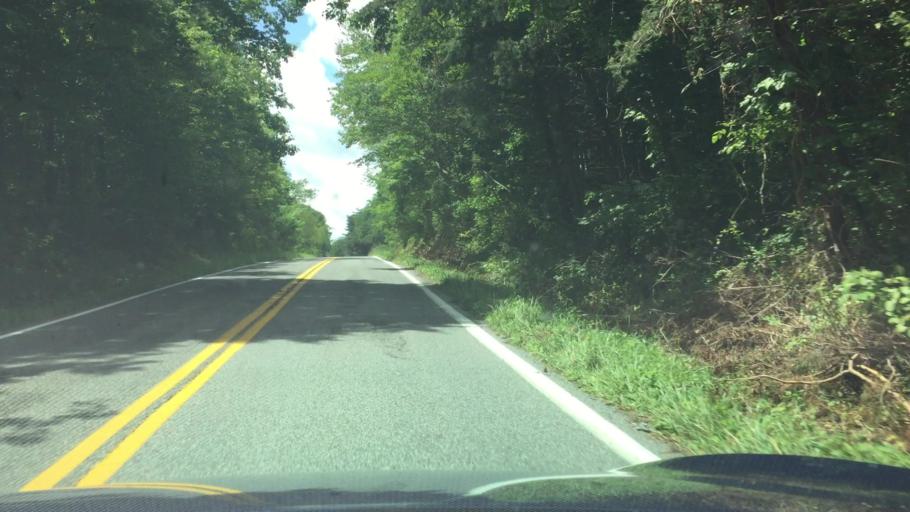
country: US
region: Virginia
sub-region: Pulaski County
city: Pulaski
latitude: 37.0119
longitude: -80.7436
